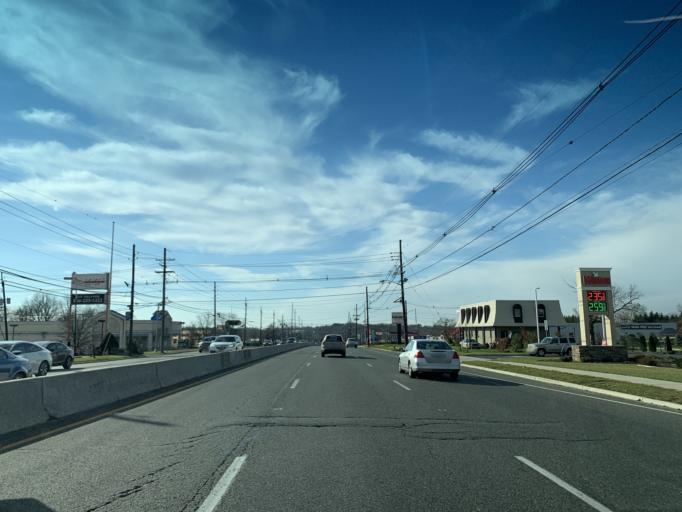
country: US
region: New Jersey
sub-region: Burlington County
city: Cinnaminson
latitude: 40.0077
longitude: -74.9721
